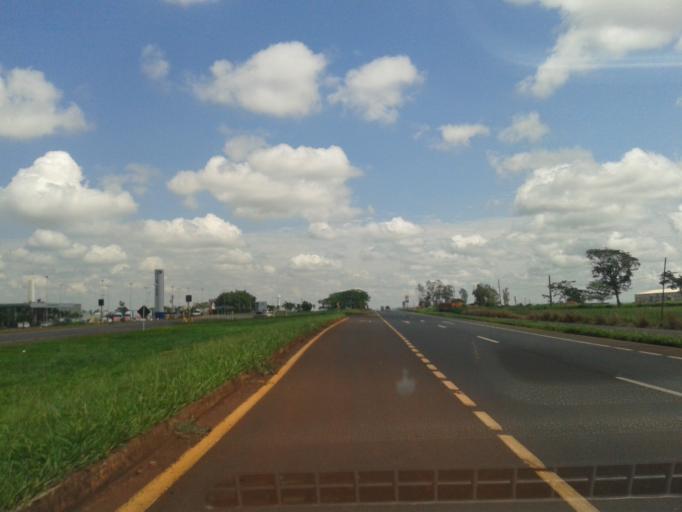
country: BR
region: Minas Gerais
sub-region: Centralina
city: Centralina
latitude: -18.5774
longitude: -49.1936
